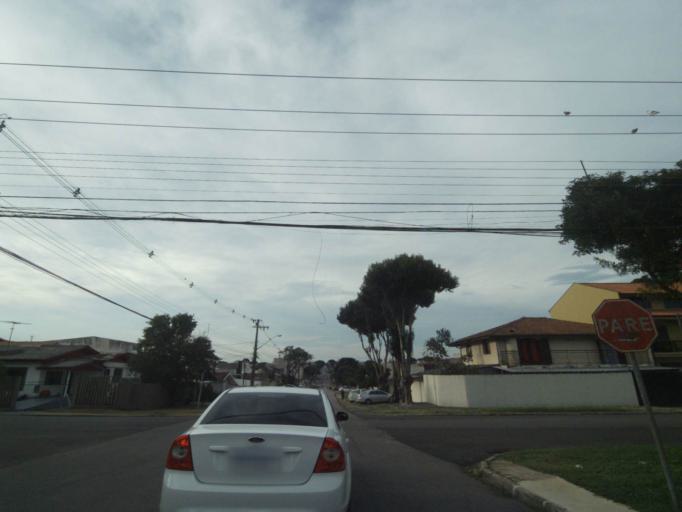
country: BR
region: Parana
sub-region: Pinhais
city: Pinhais
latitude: -25.4589
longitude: -49.2174
